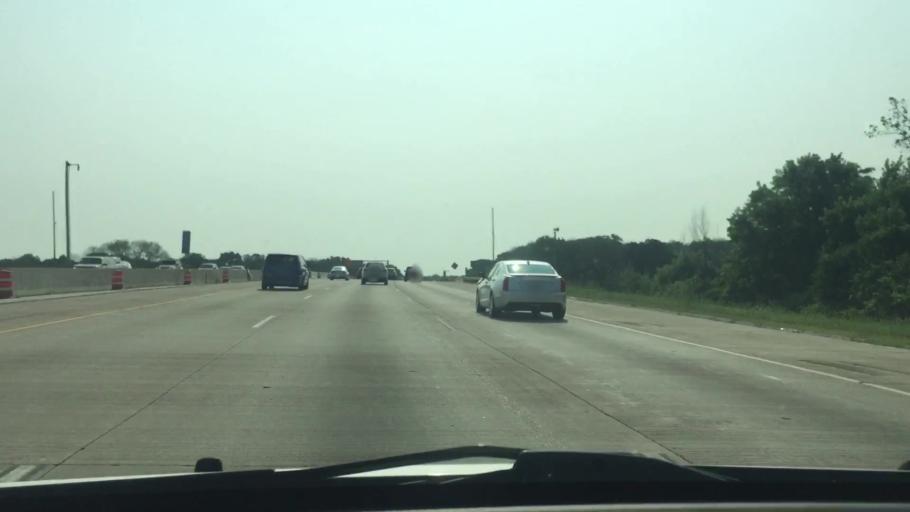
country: US
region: Wisconsin
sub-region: Waukesha County
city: Brookfield
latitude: 43.0281
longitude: -88.1292
